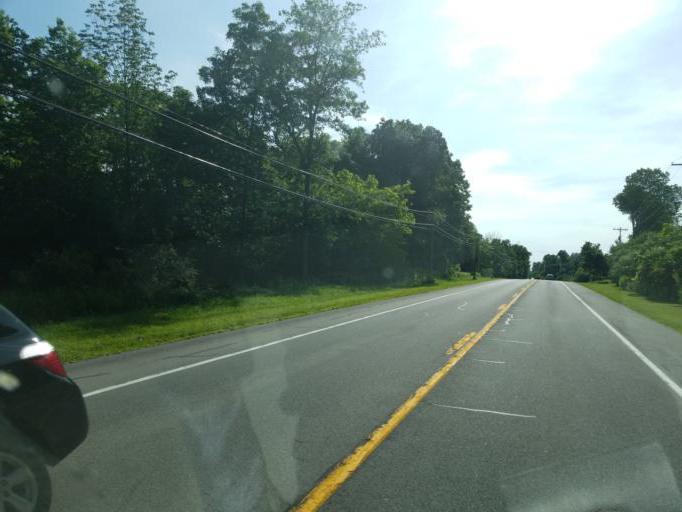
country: US
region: New York
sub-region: Livingston County
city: Caledonia
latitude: 42.9790
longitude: -77.8990
